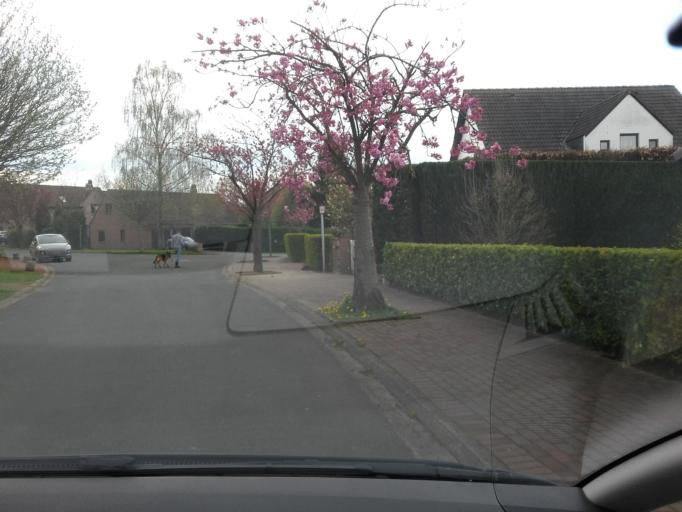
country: BE
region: Wallonia
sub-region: Province du Brabant Wallon
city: Waterloo
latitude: 50.6995
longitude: 4.4190
